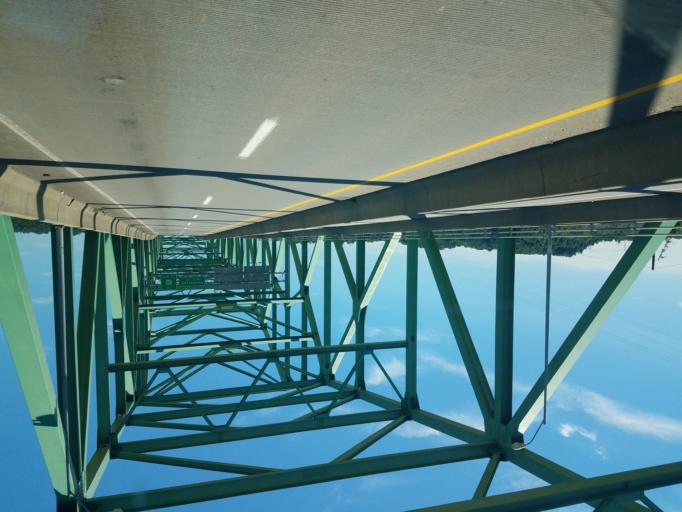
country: US
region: West Virginia
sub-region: Mason County
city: Point Pleasant
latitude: 38.8390
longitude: -82.1389
